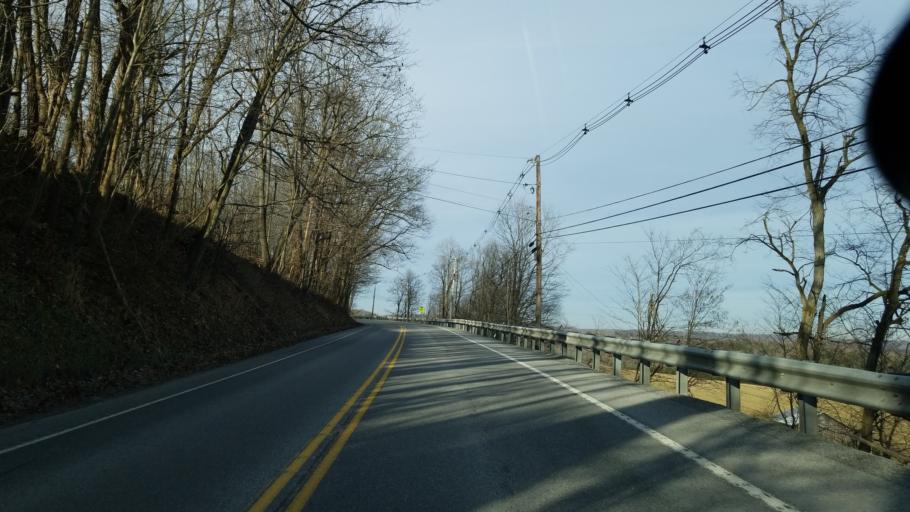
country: US
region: Pennsylvania
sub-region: Clearfield County
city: Curwensville
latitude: 40.9948
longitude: -78.6294
